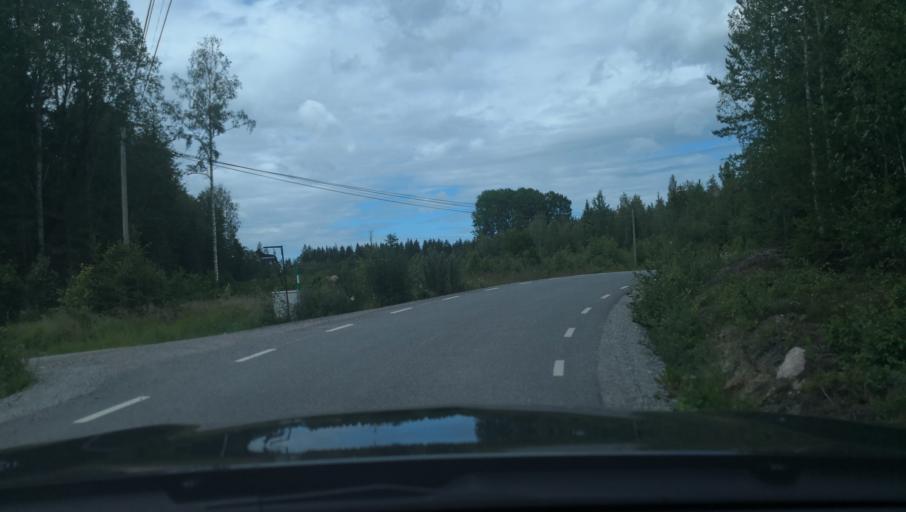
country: SE
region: Vaestmanland
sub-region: Hallstahammars Kommun
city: Hallstahammar
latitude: 59.6213
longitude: 16.1400
